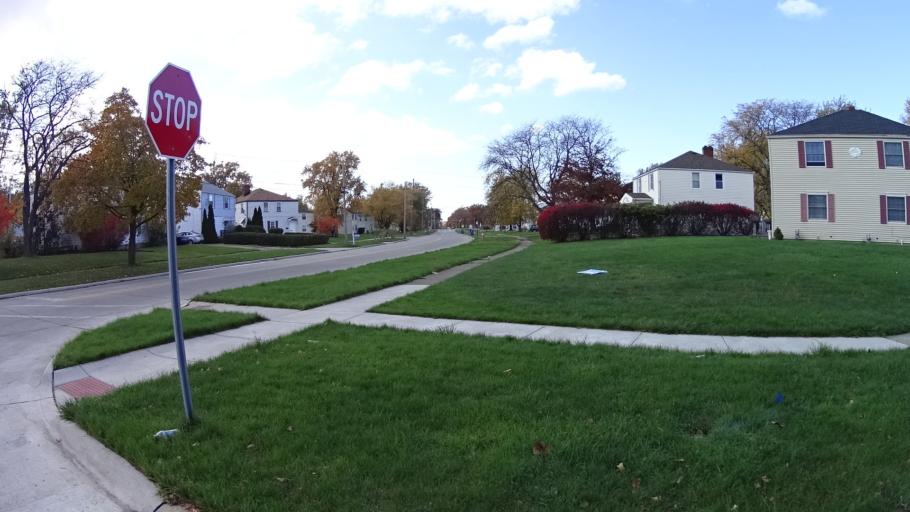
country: US
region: Ohio
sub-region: Lorain County
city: Sheffield
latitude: 41.4361
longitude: -82.1150
